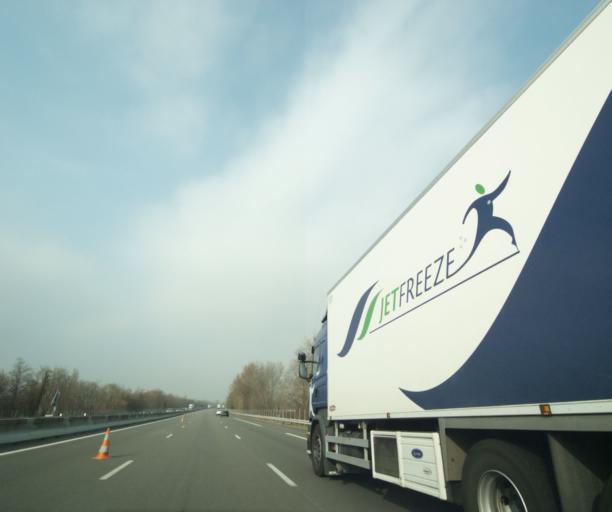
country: FR
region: Rhone-Alpes
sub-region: Departement de la Drome
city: La Roche-de-Glun
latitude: 44.9927
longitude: 4.8801
